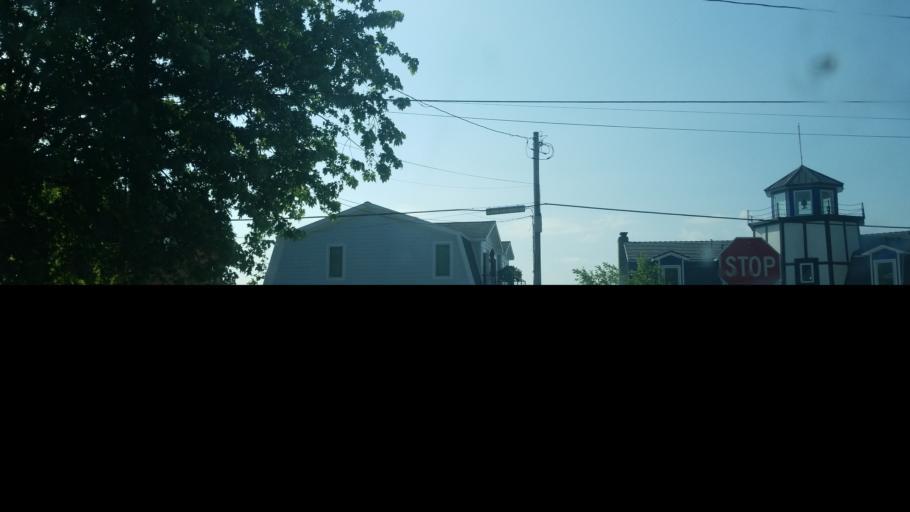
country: US
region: Ohio
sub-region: Logan County
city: Russells Point
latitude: 40.4877
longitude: -83.8768
